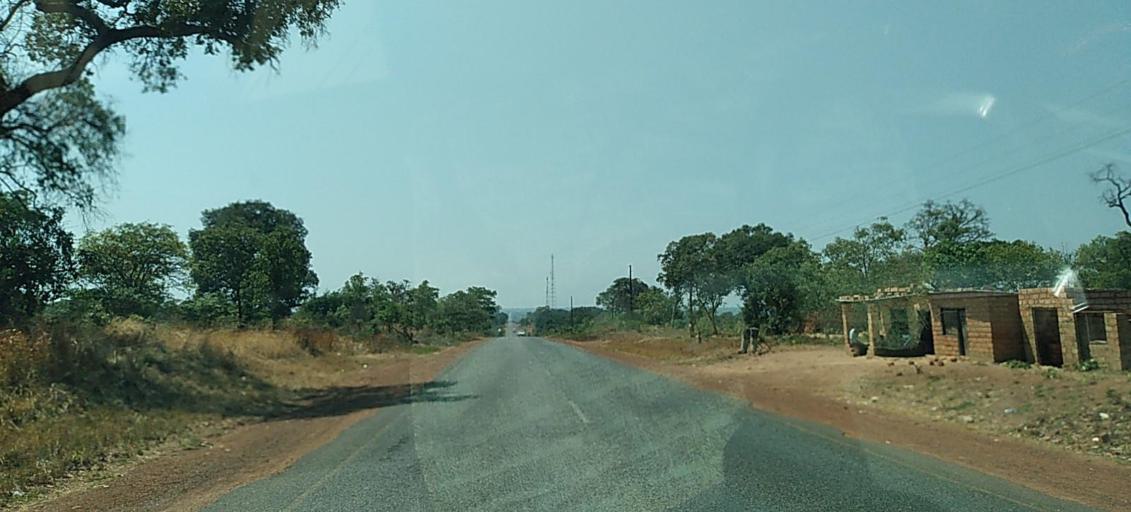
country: ZM
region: North-Western
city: Solwezi
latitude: -12.3246
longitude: 25.8817
